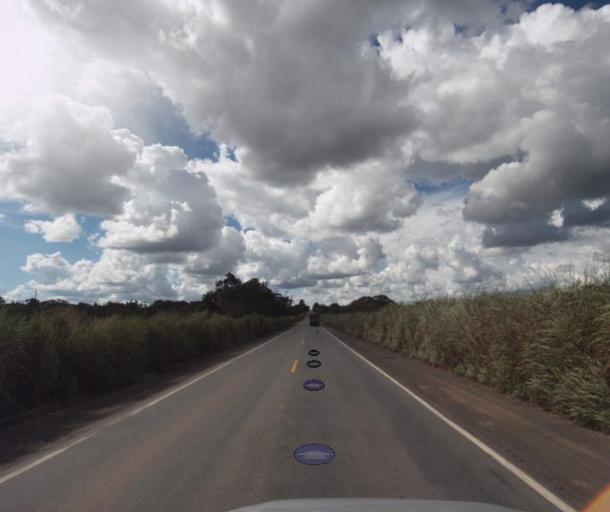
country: BR
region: Goias
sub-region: Porangatu
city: Porangatu
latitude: -13.3319
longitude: -49.1202
